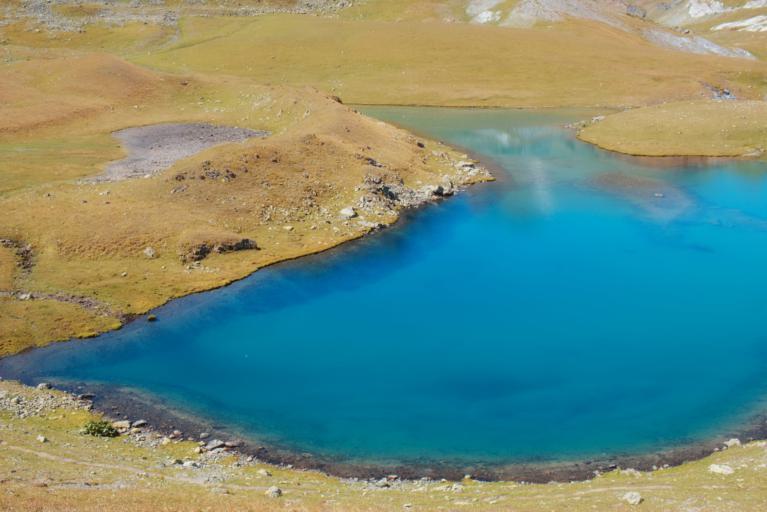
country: RU
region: Karachayevo-Cherkesiya
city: Nizhniy Arkhyz
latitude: 43.6046
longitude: 41.1628
